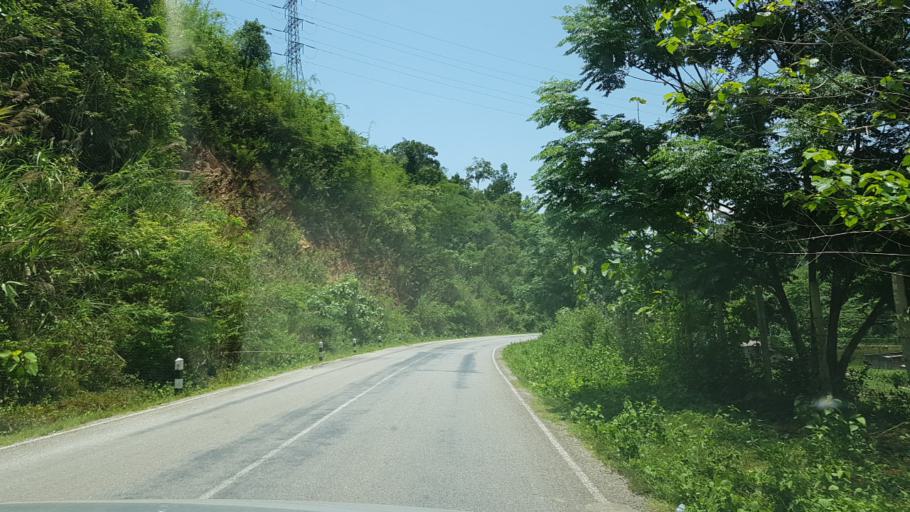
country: LA
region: Vientiane
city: Muang Kasi
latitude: 19.2712
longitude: 102.2099
